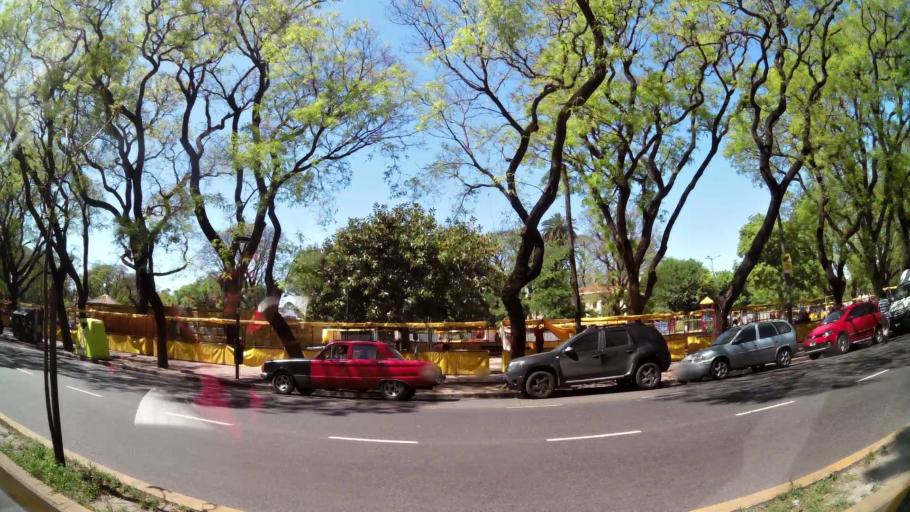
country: AR
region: Buenos Aires F.D.
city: Buenos Aires
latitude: -34.6380
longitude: -58.4103
